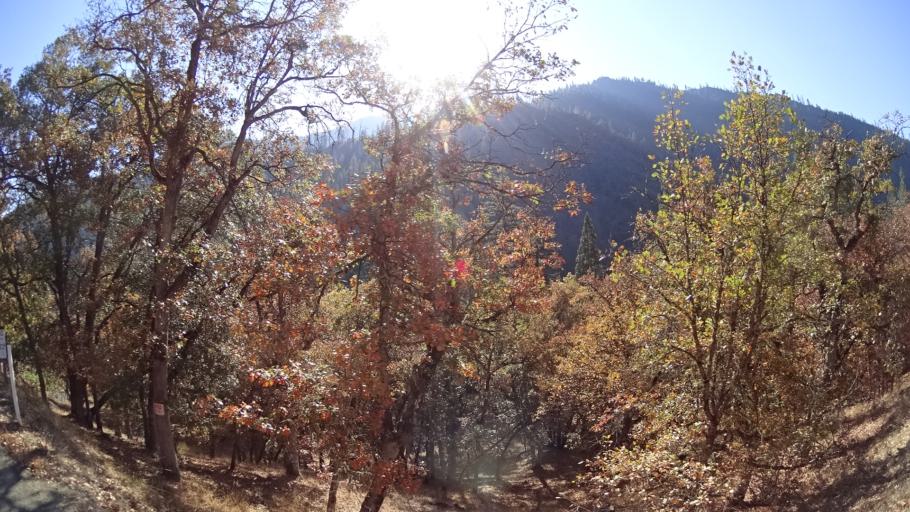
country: US
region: California
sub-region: Siskiyou County
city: Happy Camp
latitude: 41.6950
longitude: -123.0644
